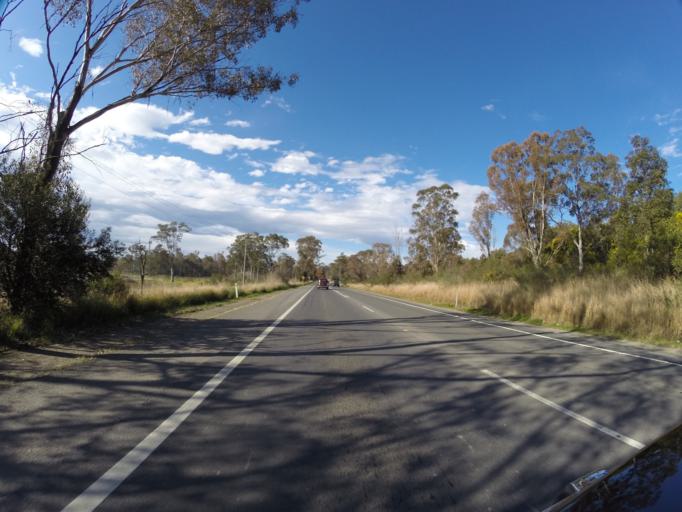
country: AU
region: New South Wales
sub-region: Fairfield
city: Cecil Park
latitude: -33.8752
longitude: 150.8364
